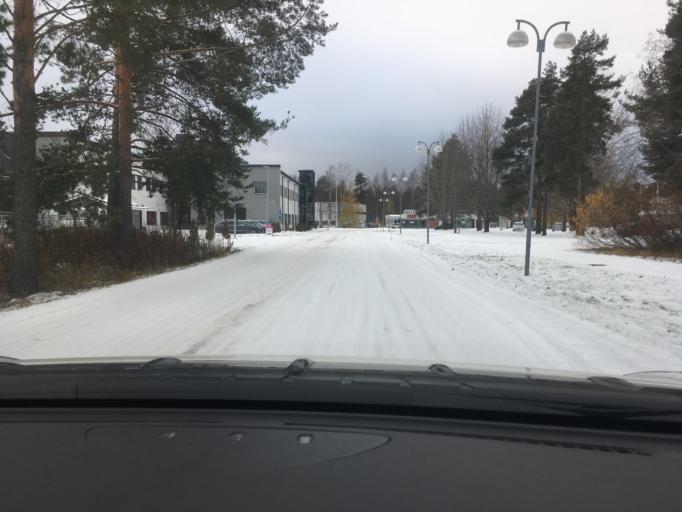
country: FI
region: North Karelia
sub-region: Joensuu
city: Joensuu
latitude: 62.6123
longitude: 29.7759
